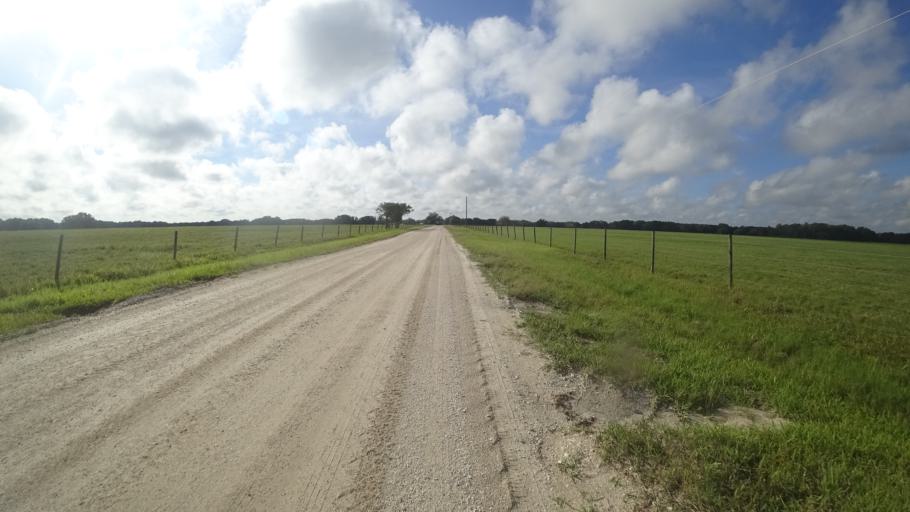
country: US
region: Florida
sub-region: Hillsborough County
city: Wimauma
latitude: 27.4721
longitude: -82.2273
